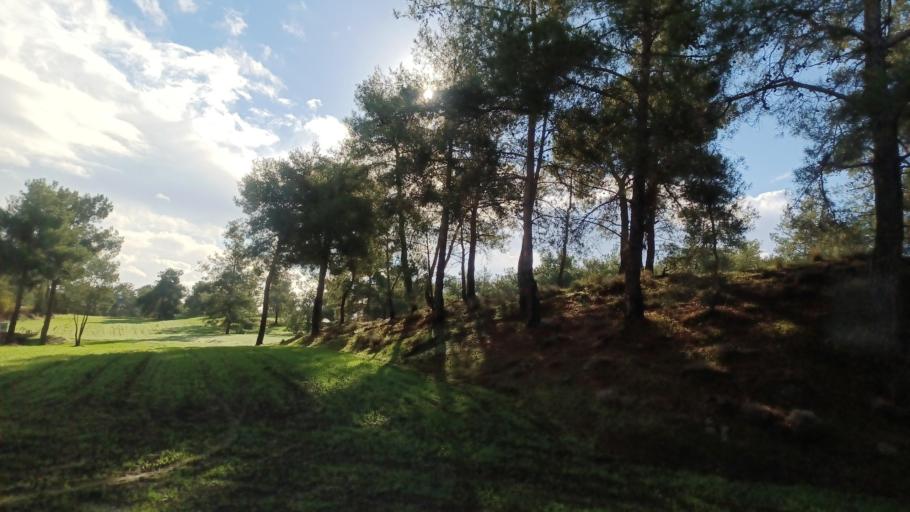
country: CY
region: Lefkosia
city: Lythrodontas
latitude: 34.9586
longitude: 33.3289
